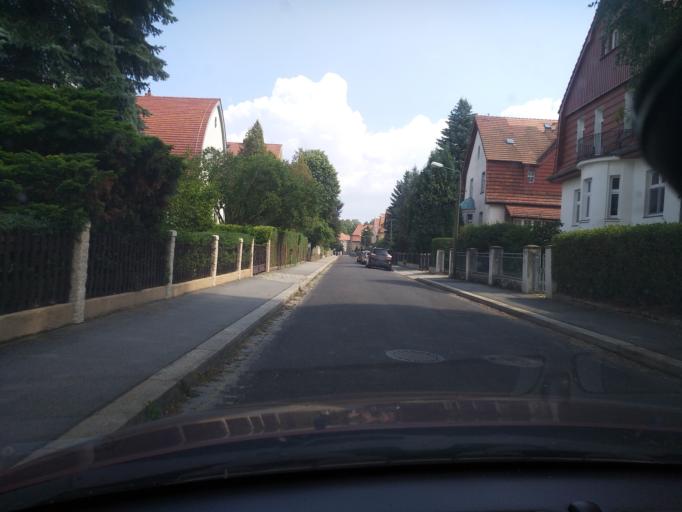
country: DE
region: Saxony
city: Goerlitz
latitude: 51.1383
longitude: 14.9752
